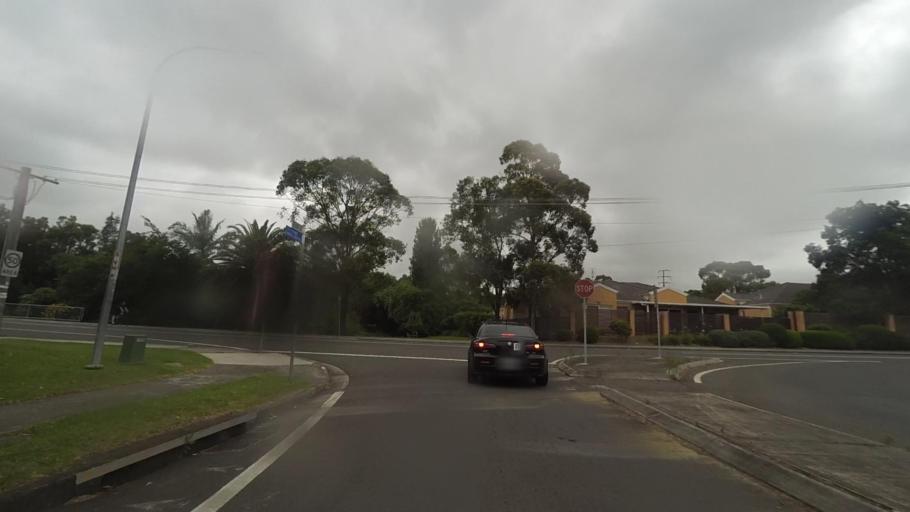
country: AU
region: New South Wales
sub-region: Wollongong
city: Cordeaux Heights
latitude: -34.4440
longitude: 150.8442
